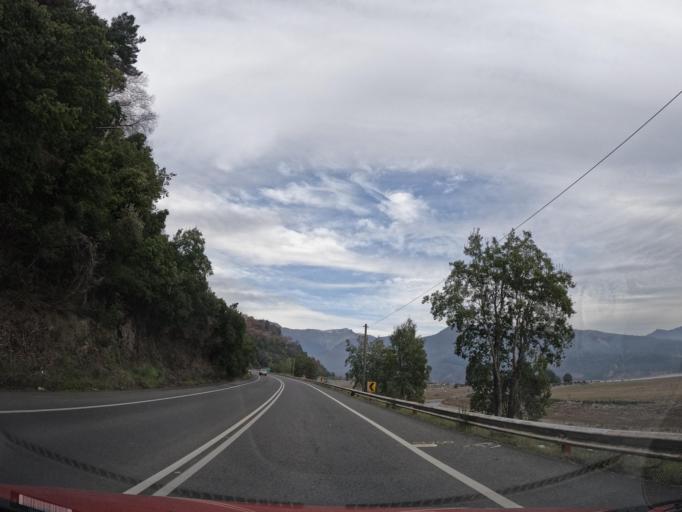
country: CL
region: Maule
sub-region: Provincia de Linares
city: Colbun
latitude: -35.7000
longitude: -71.2223
